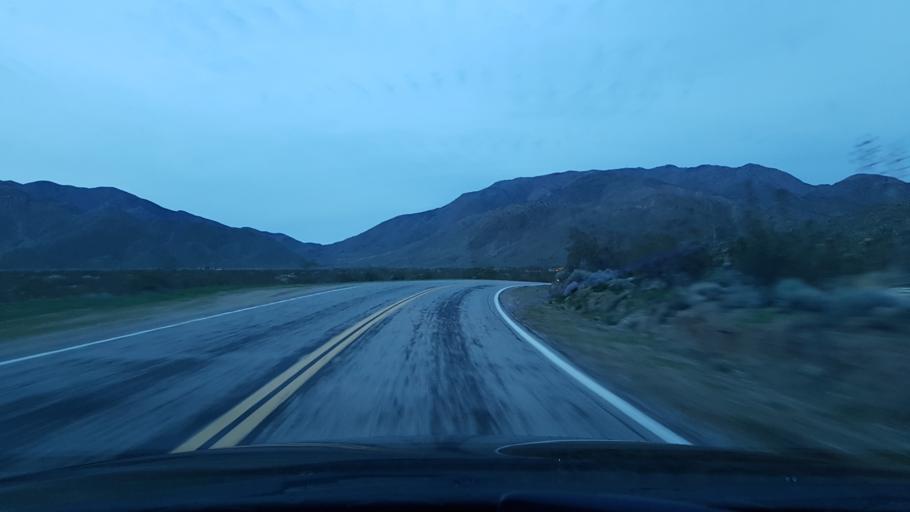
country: US
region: California
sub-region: San Diego County
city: Julian
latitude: 33.0006
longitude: -116.4516
